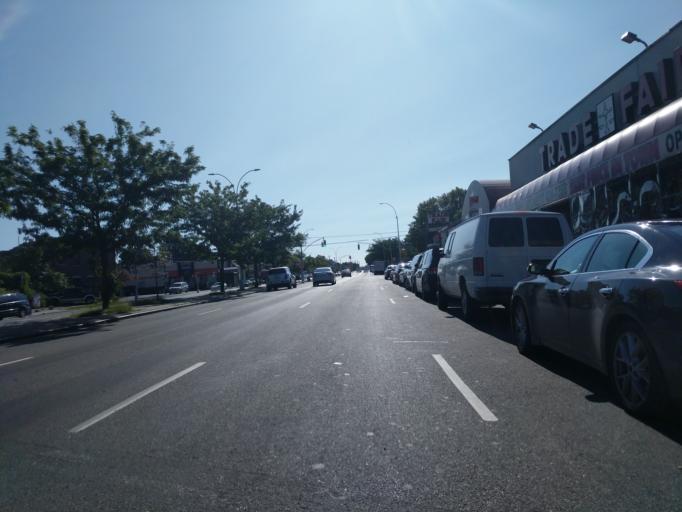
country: US
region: New York
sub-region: Queens County
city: Long Island City
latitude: 40.7621
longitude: -73.8703
